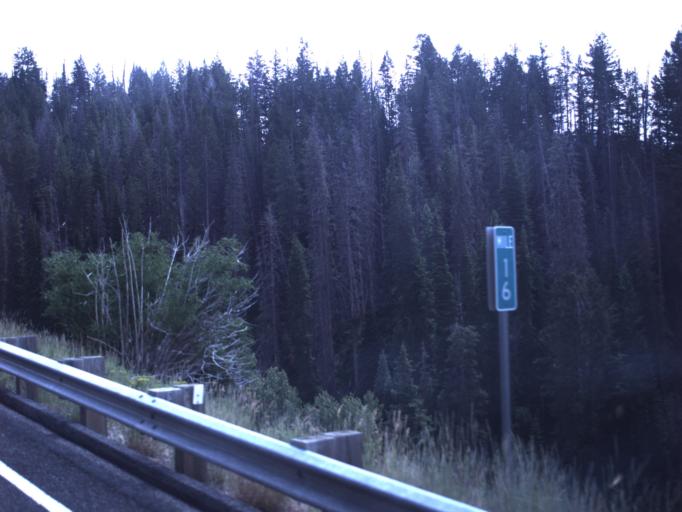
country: US
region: Utah
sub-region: Summit County
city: Francis
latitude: 40.5157
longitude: -111.0562
